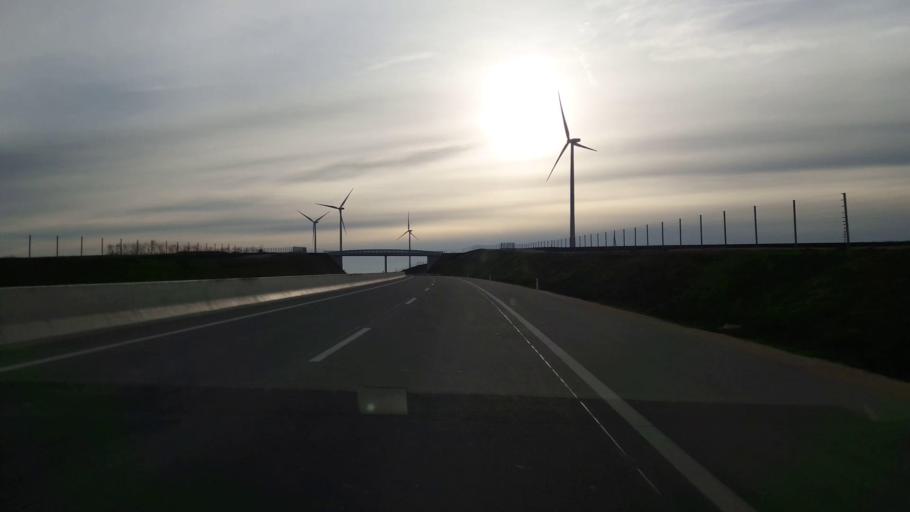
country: AT
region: Lower Austria
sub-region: Politischer Bezirk Mistelbach
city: Grosskrut
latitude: 48.6323
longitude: 16.6788
